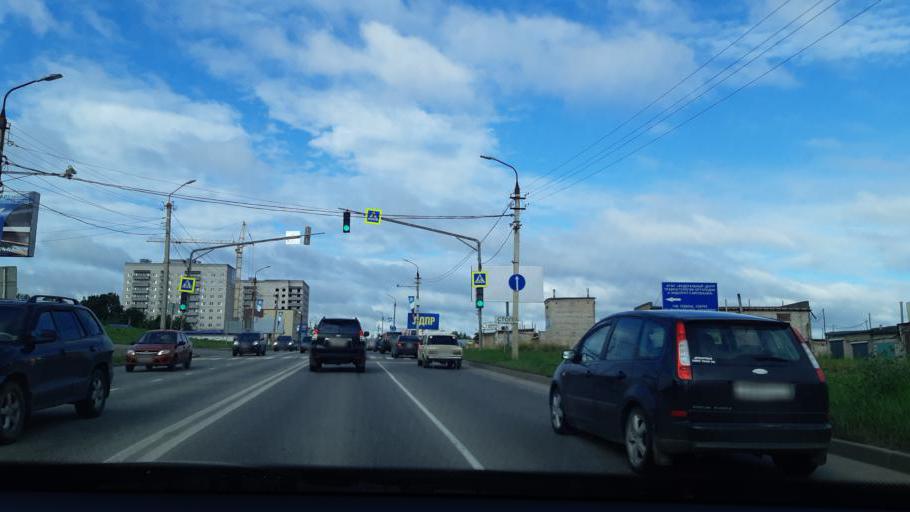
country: RU
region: Smolensk
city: Smolensk
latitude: 54.7591
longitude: 32.0799
